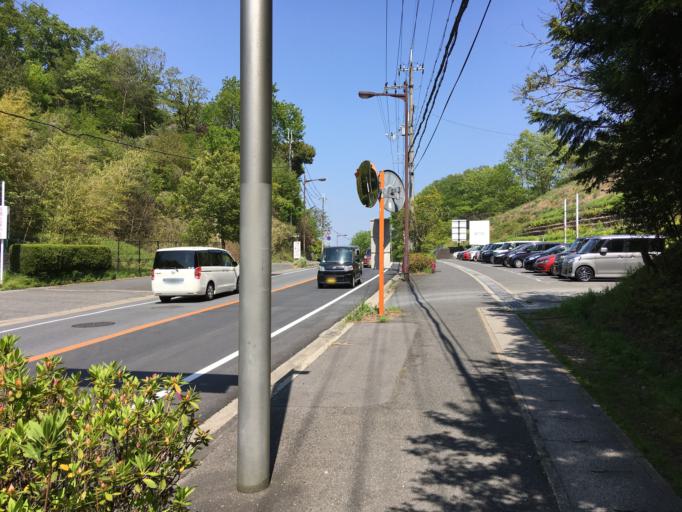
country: JP
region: Nara
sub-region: Ikoma-shi
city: Ikoma
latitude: 34.6863
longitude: 135.7191
